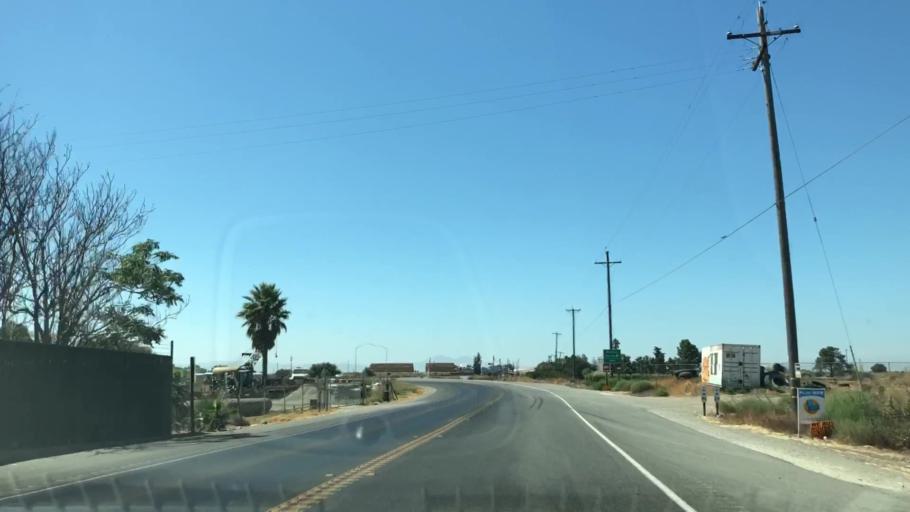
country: US
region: California
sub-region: San Joaquin County
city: Country Club
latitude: 37.9269
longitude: -121.4262
